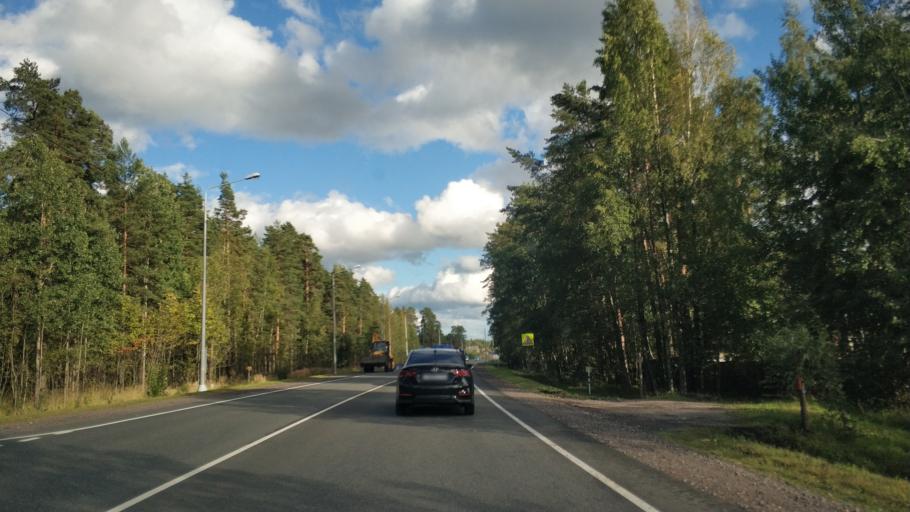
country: RU
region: Leningrad
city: Priozersk
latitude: 61.0087
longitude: 30.1715
